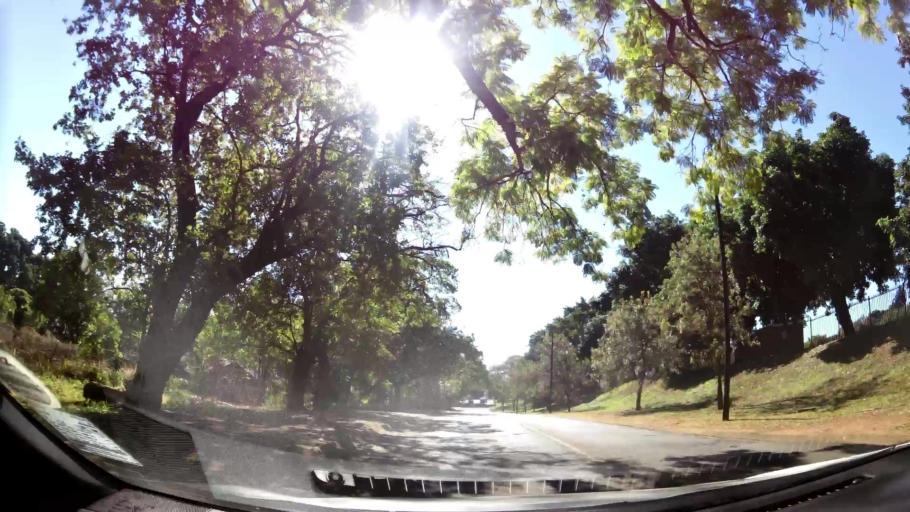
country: ZA
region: Limpopo
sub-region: Mopani District Municipality
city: Tzaneen
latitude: -23.8302
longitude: 30.1533
